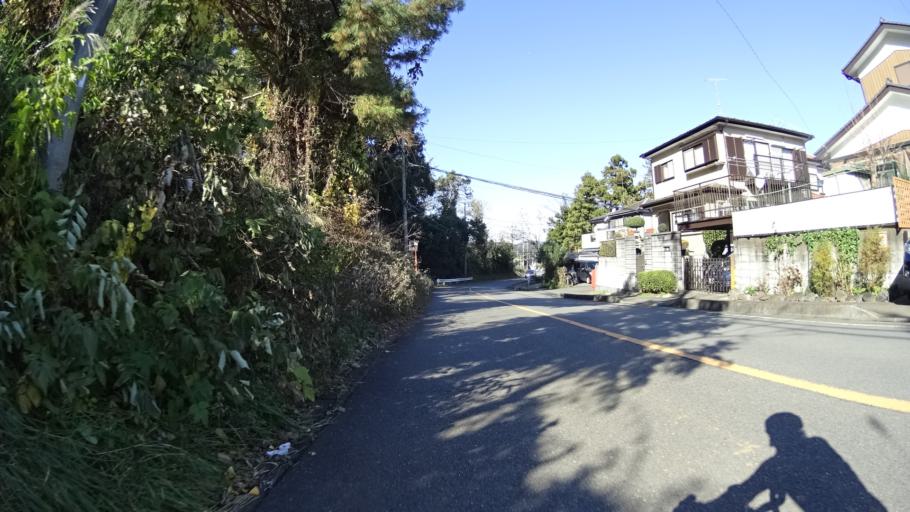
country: JP
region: Kanagawa
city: Zama
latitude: 35.5314
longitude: 139.2696
